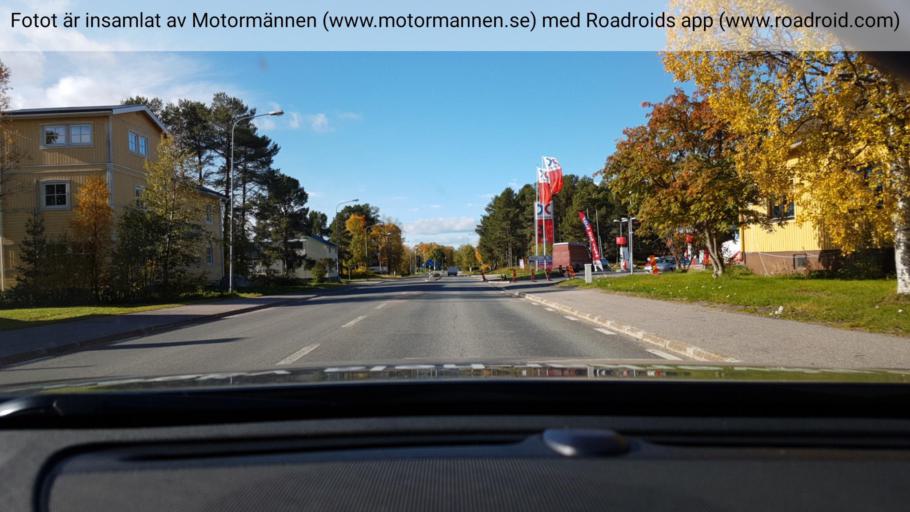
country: SE
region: Norrbotten
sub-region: Arjeplogs Kommun
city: Arjeplog
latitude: 66.0511
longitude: 17.9003
